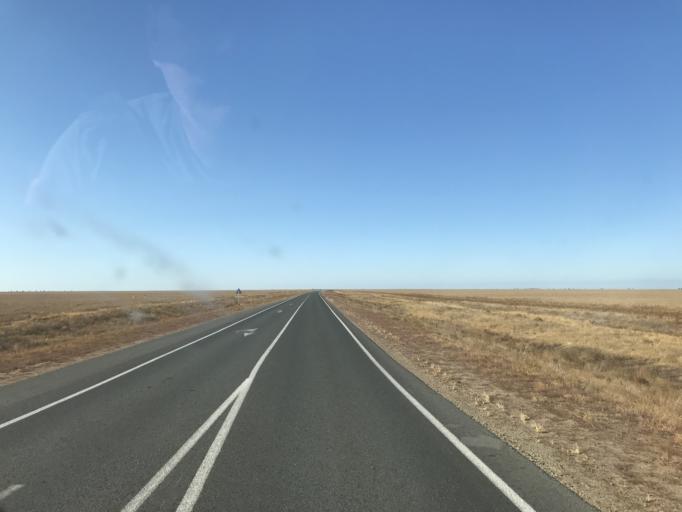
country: KZ
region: Pavlodar
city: Kurchatov
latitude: 51.2059
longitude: 78.6606
